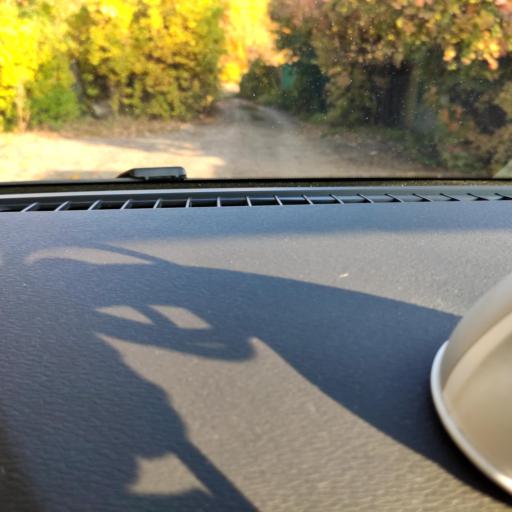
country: RU
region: Samara
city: Petra-Dubrava
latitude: 53.2598
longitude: 50.2735
